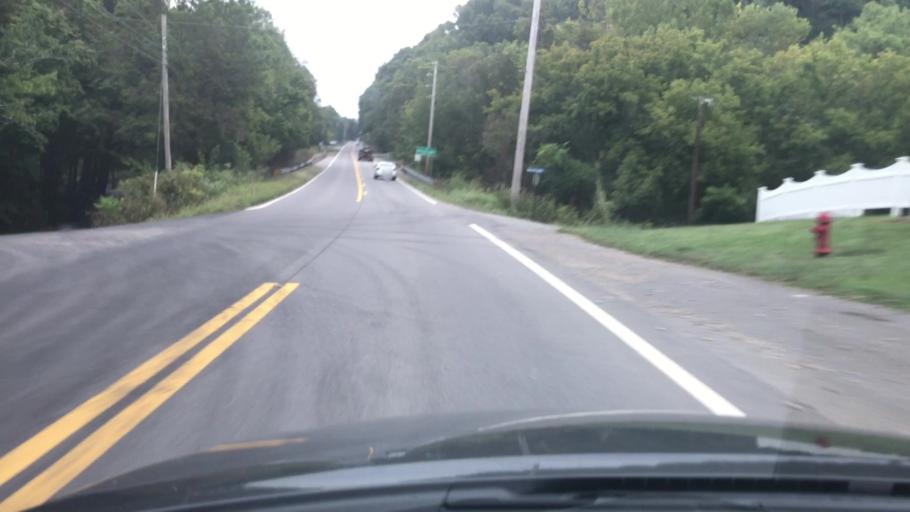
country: US
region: Tennessee
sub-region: Cheatham County
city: Ashland City
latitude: 36.2808
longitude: -87.1034
